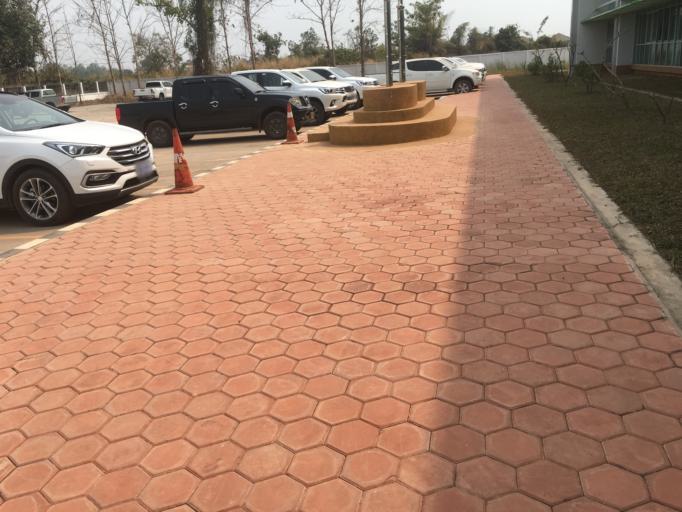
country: LA
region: Vientiane
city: Vientiane
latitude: 17.9624
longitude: 102.6705
